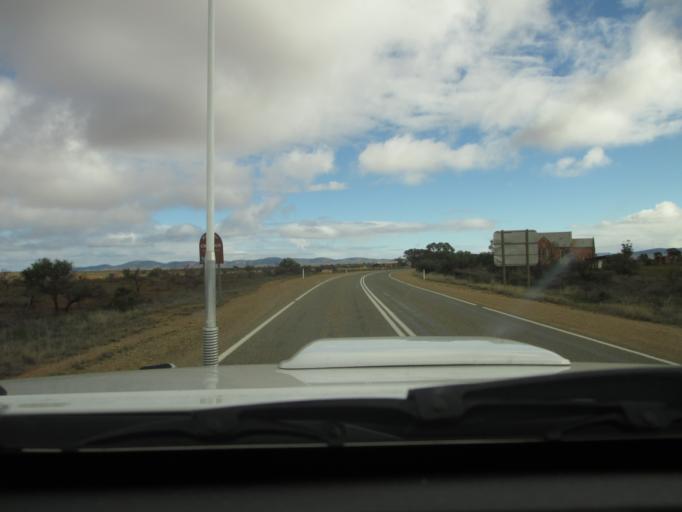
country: AU
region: South Australia
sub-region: Flinders Ranges
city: Quorn
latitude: -32.0734
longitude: 138.4966
